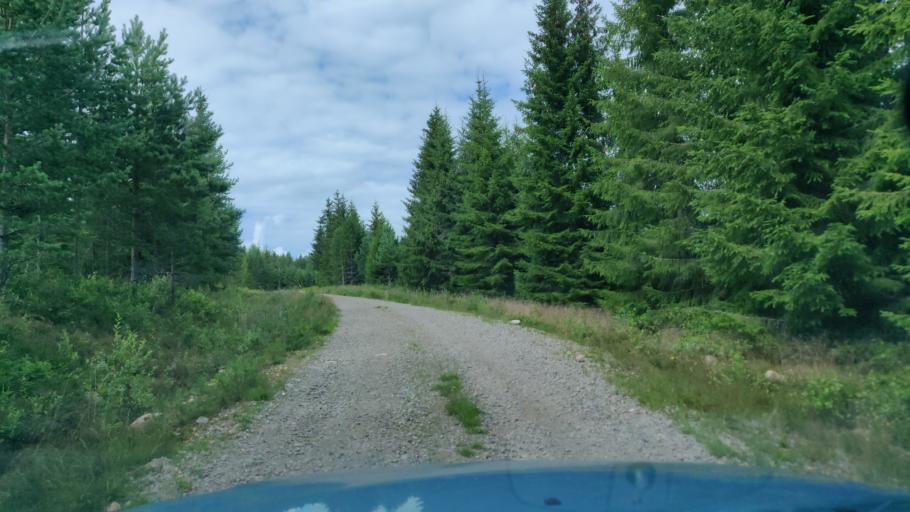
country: SE
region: Vaermland
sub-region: Hagfors Kommun
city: Hagfors
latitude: 59.9459
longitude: 13.5967
